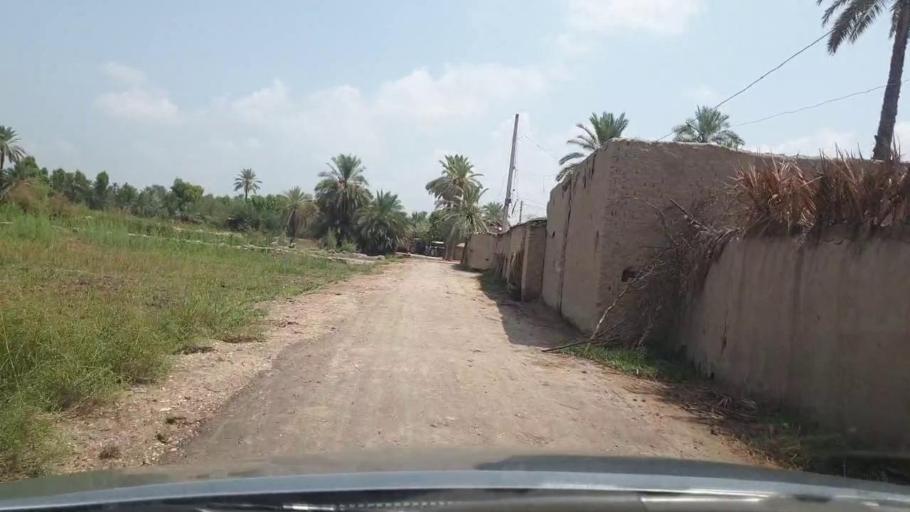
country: PK
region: Sindh
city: Pir jo Goth
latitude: 27.6236
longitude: 68.6654
